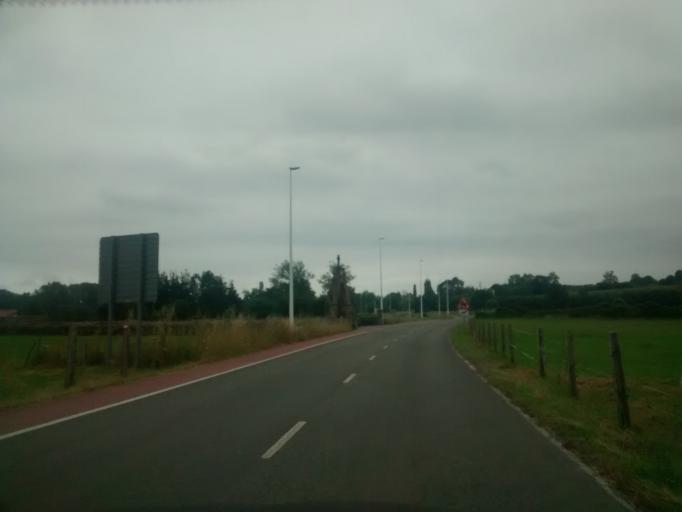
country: ES
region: Cantabria
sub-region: Provincia de Cantabria
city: Luzmela
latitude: 43.2926
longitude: -4.2192
